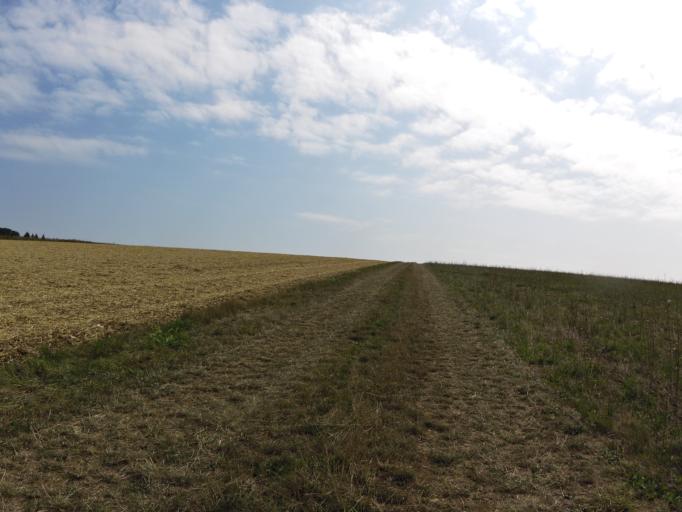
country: DE
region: Bavaria
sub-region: Regierungsbezirk Unterfranken
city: Waldbrunn
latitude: 49.7106
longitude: 9.7946
